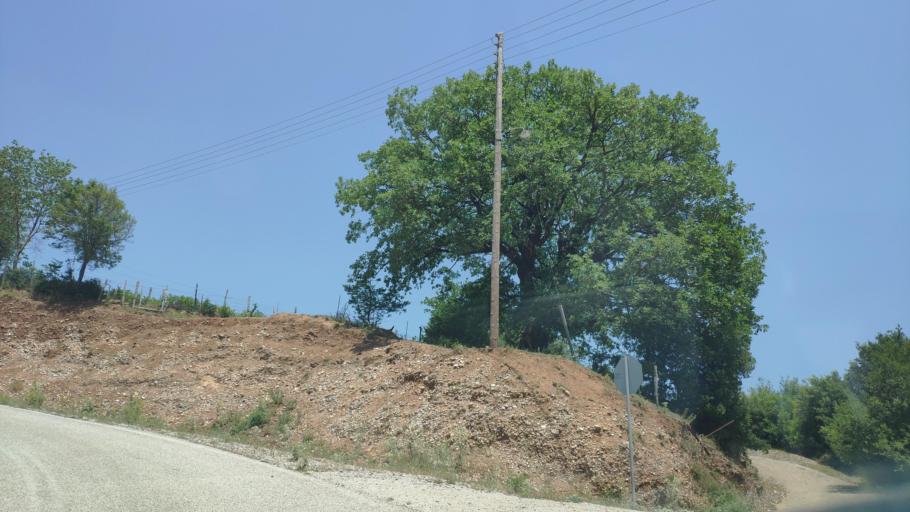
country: GR
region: Thessaly
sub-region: Nomos Kardhitsas
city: Anthiro
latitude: 39.2195
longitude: 21.3501
